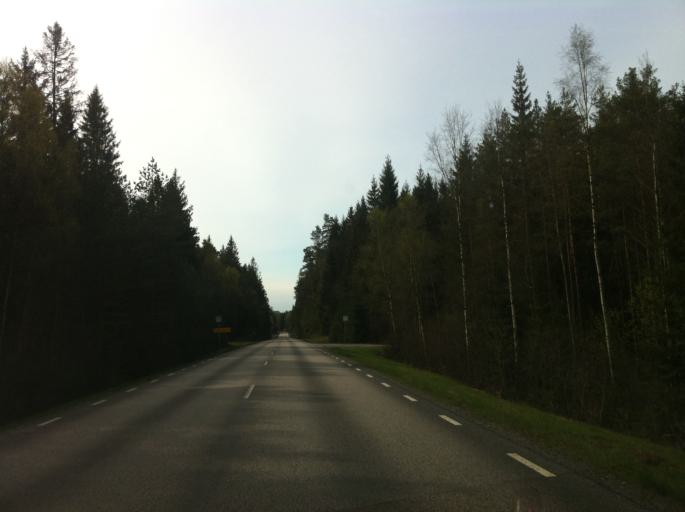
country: SE
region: Vaestra Goetaland
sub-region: Marks Kommun
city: Kinna
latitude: 57.4133
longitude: 12.7742
